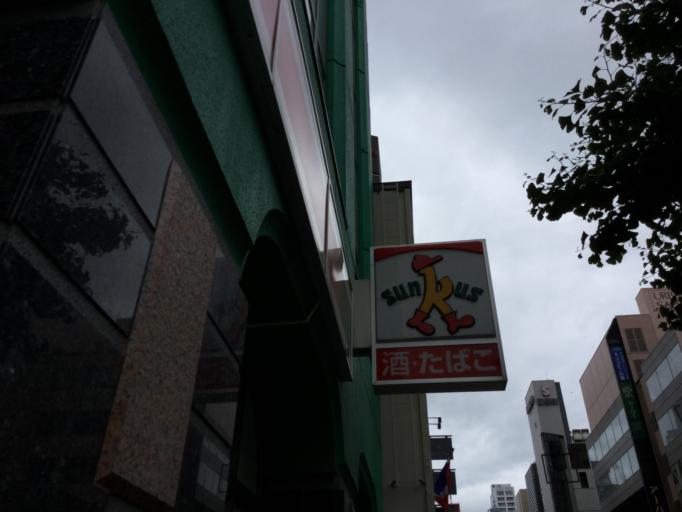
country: JP
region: Hokkaido
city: Sapporo
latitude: 43.0555
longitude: 141.3516
